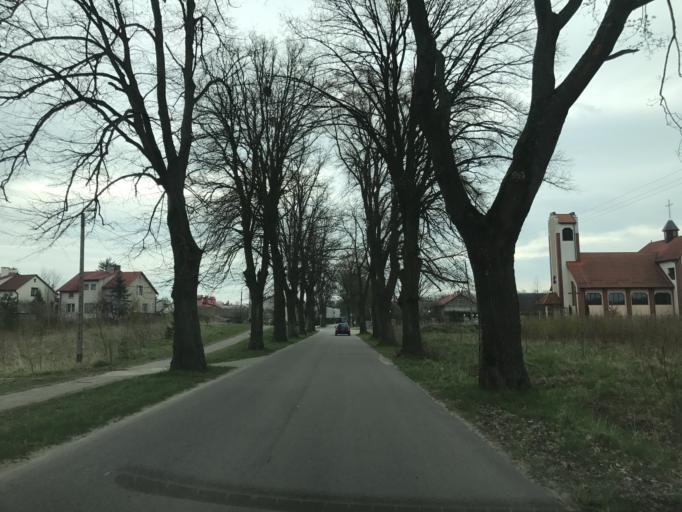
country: PL
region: Warmian-Masurian Voivodeship
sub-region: Powiat olsztynski
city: Olsztynek
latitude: 53.5891
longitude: 20.2784
